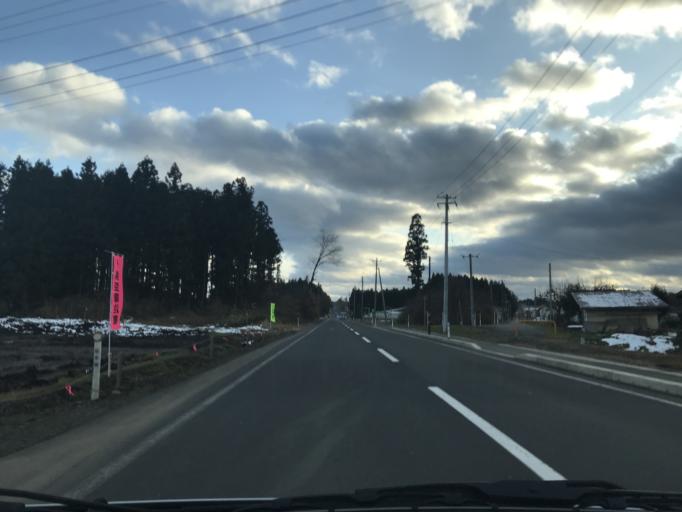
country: JP
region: Iwate
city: Mizusawa
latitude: 39.1014
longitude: 141.0514
